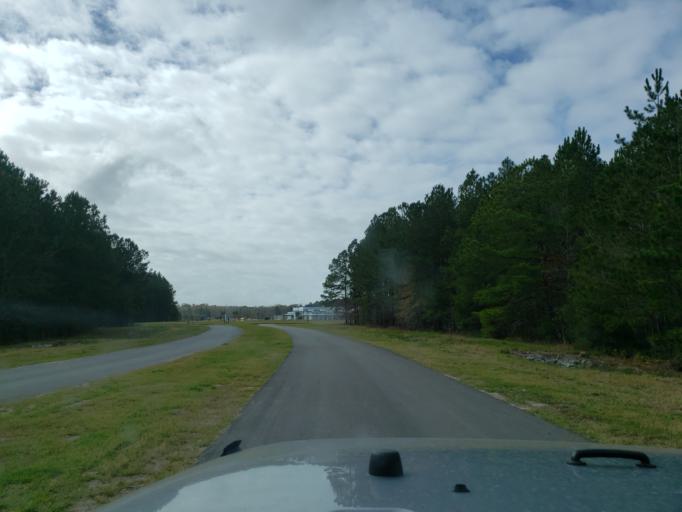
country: US
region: Georgia
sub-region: Chatham County
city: Port Wentworth
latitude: 32.2208
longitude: -81.1915
